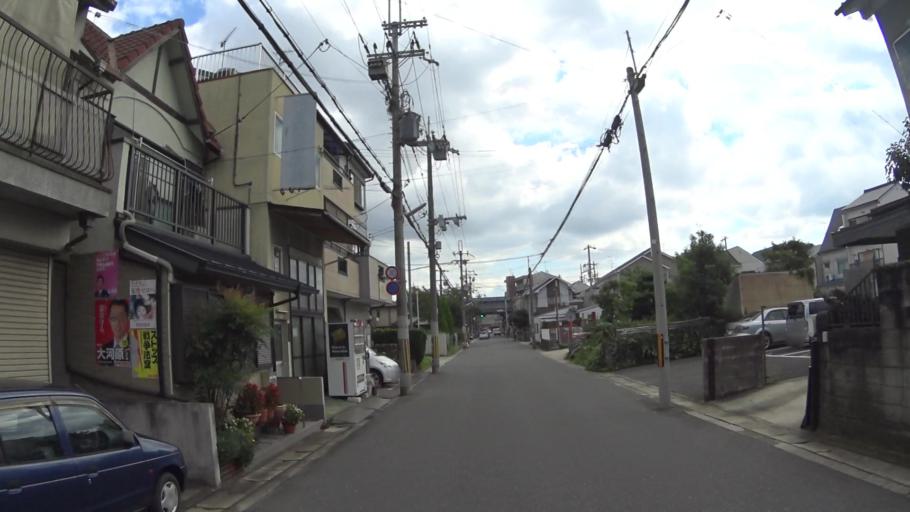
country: JP
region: Kyoto
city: Muko
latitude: 34.9578
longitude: 135.7132
